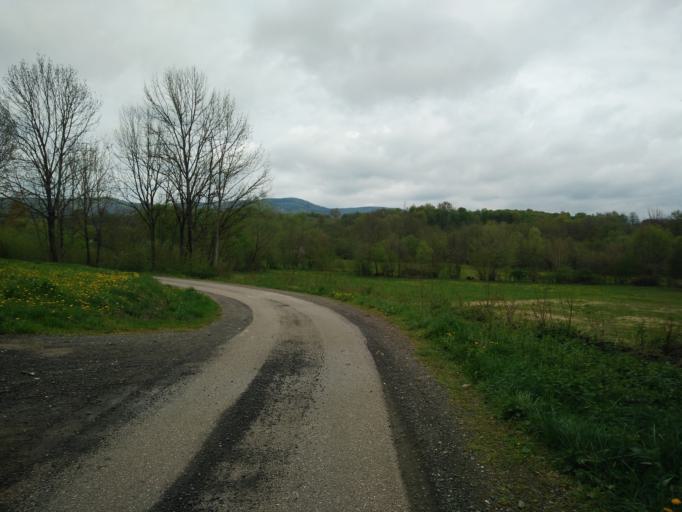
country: BA
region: Republika Srpska
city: Prijedor
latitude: 45.0014
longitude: 16.7512
